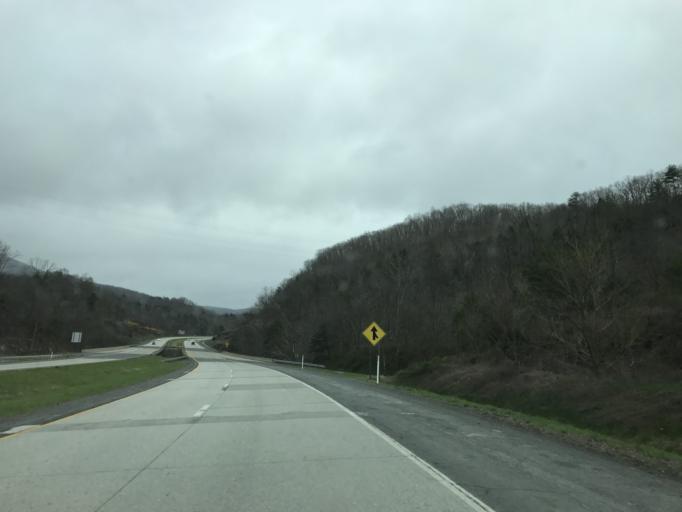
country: US
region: West Virginia
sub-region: Summers County
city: Hinton
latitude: 37.7815
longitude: -80.8923
